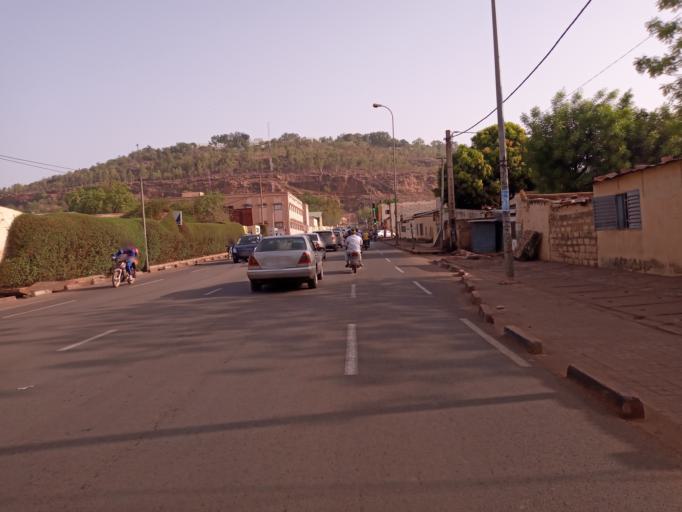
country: ML
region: Bamako
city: Bamako
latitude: 12.6517
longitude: -8.0079
